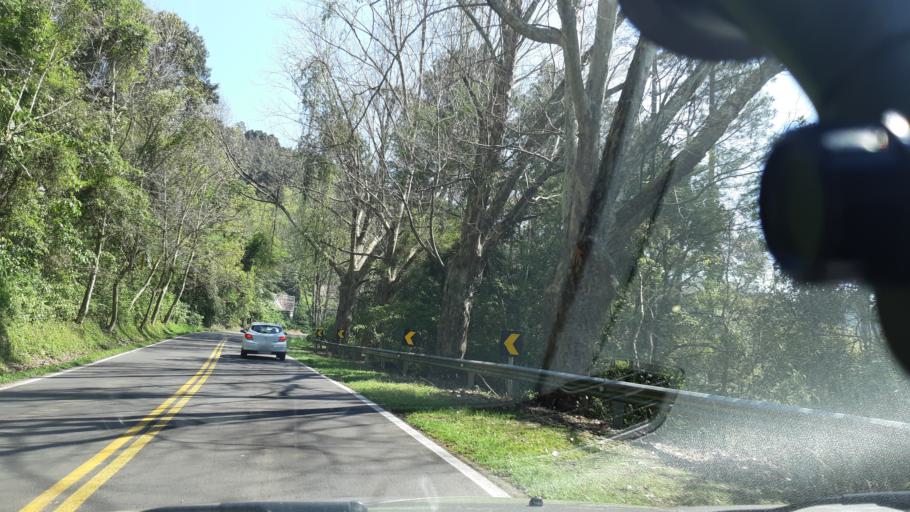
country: BR
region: Rio Grande do Sul
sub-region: Nova Petropolis
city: Nova Petropolis
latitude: -29.4022
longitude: -51.1255
